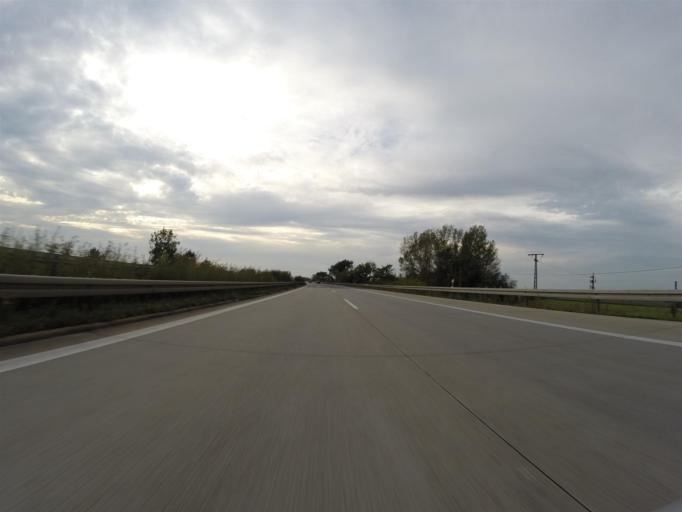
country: DE
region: Saxony
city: Nossen
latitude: 51.0786
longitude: 13.3027
